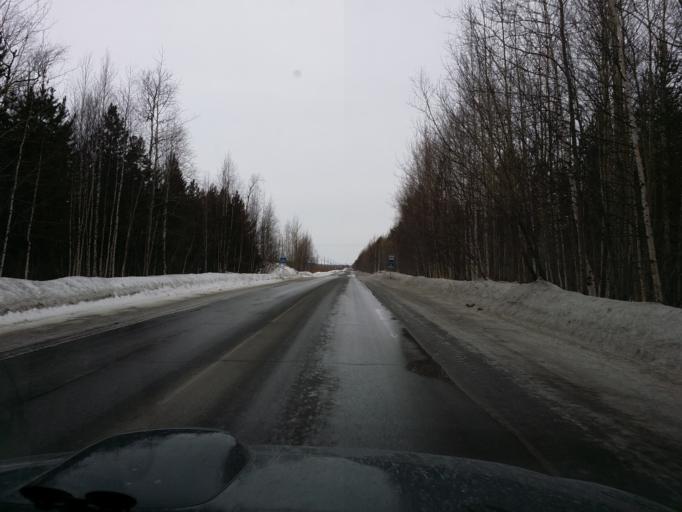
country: RU
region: Tomsk
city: Strezhevoy
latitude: 60.8006
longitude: 77.2960
